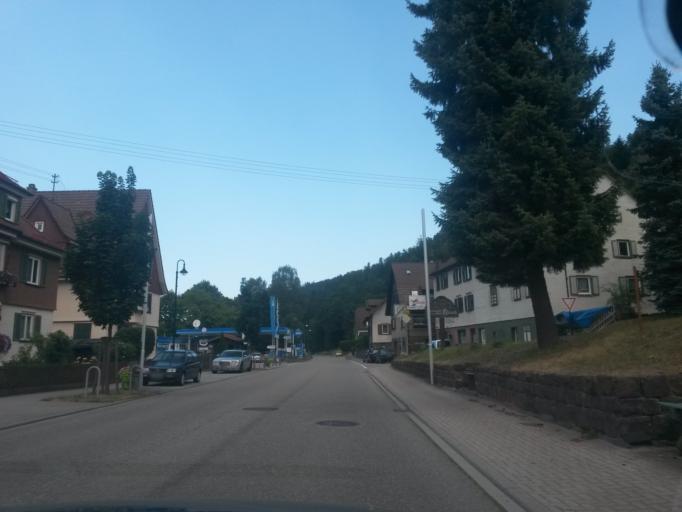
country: DE
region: Baden-Wuerttemberg
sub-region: Karlsruhe Region
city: Hofen an der Enz
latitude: 48.8068
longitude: 8.5840
